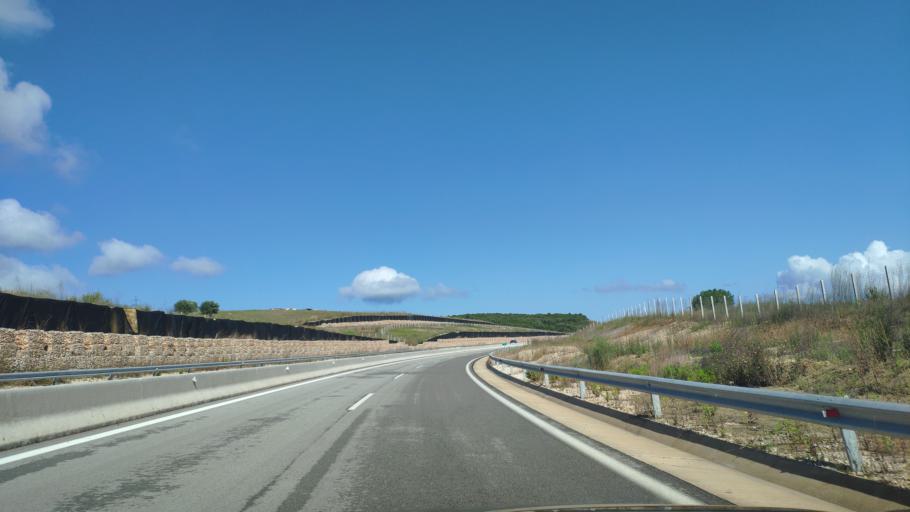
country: GR
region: West Greece
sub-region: Nomos Aitolias kai Akarnanias
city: Vonitsa
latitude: 38.9103
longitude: 20.8332
